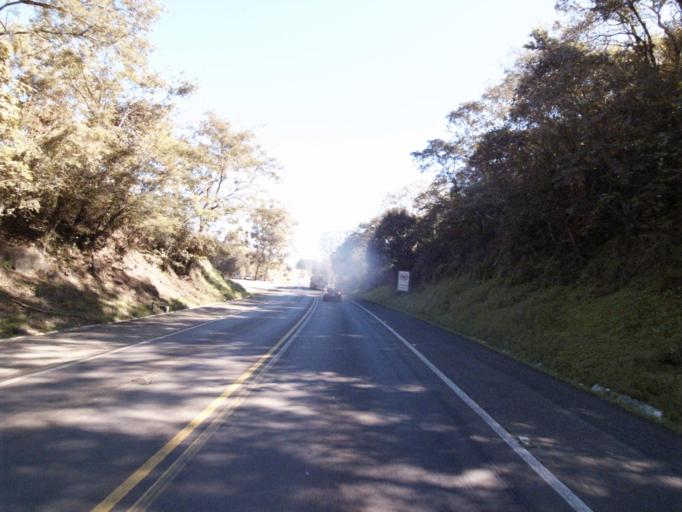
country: BR
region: Rio Grande do Sul
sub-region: Frederico Westphalen
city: Frederico Westphalen
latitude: -26.7980
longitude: -53.3423
